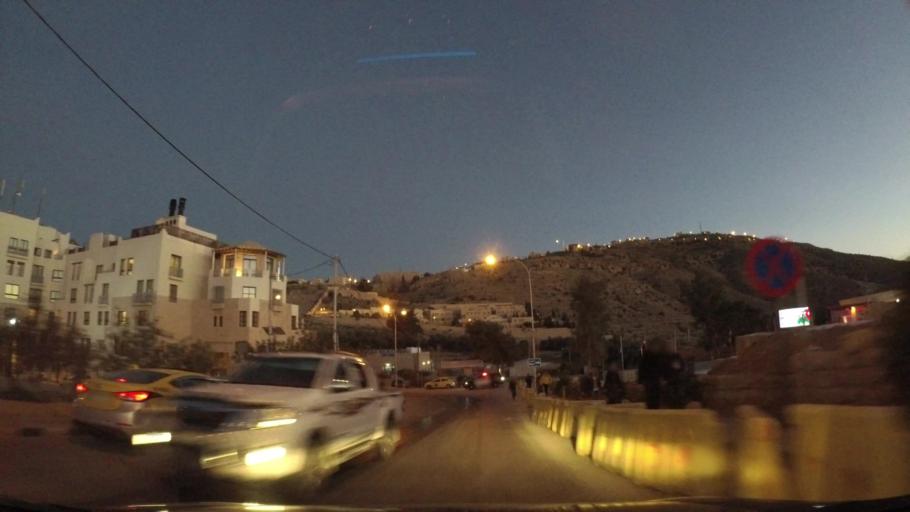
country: JO
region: Ma'an
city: Petra
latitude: 30.3254
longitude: 35.4686
